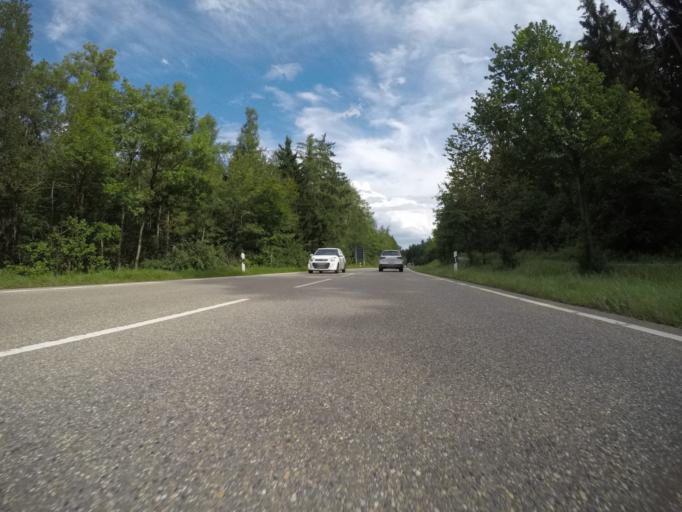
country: DE
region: Baden-Wuerttemberg
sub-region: Karlsruhe Region
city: Dornstetten
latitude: 48.4684
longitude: 8.5251
